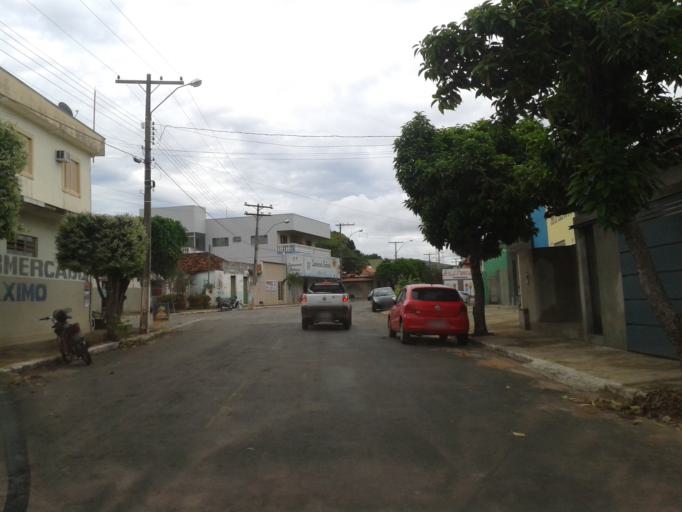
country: BR
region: Goias
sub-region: Caldas Novas
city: Caldas Novas
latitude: -17.9821
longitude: -48.6419
